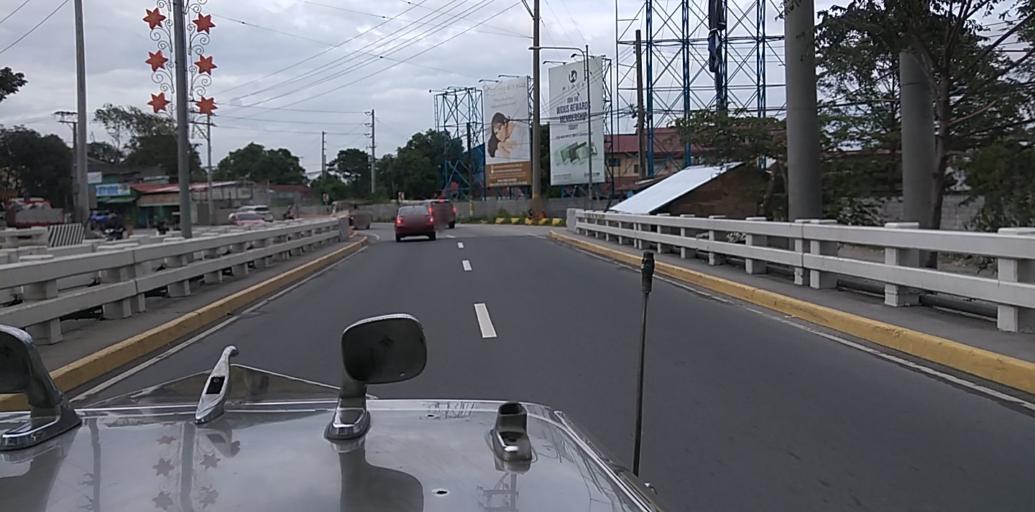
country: PH
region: Central Luzon
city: Santol
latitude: 15.1575
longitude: 120.5599
